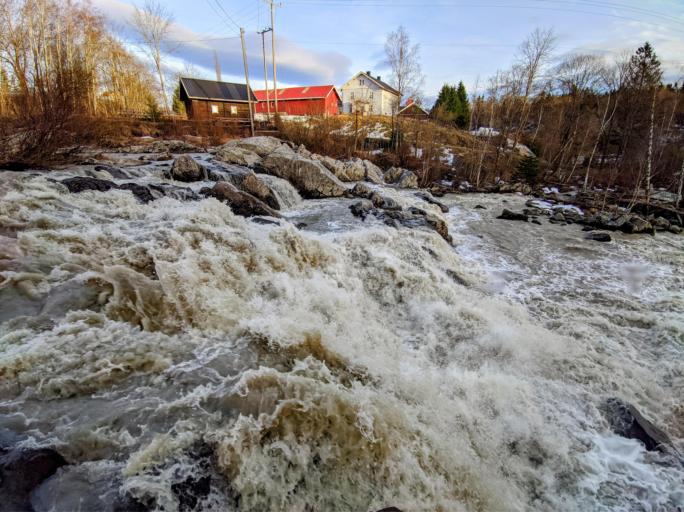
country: NO
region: Akershus
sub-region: Gjerdrum
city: Ask
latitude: 60.1323
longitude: 11.0800
